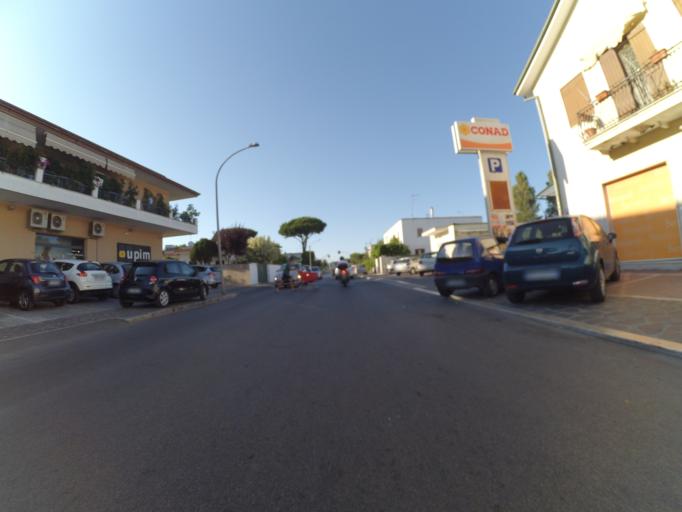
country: IT
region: Latium
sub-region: Provincia di Latina
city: San Felice Circeo
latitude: 41.2458
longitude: 13.0927
